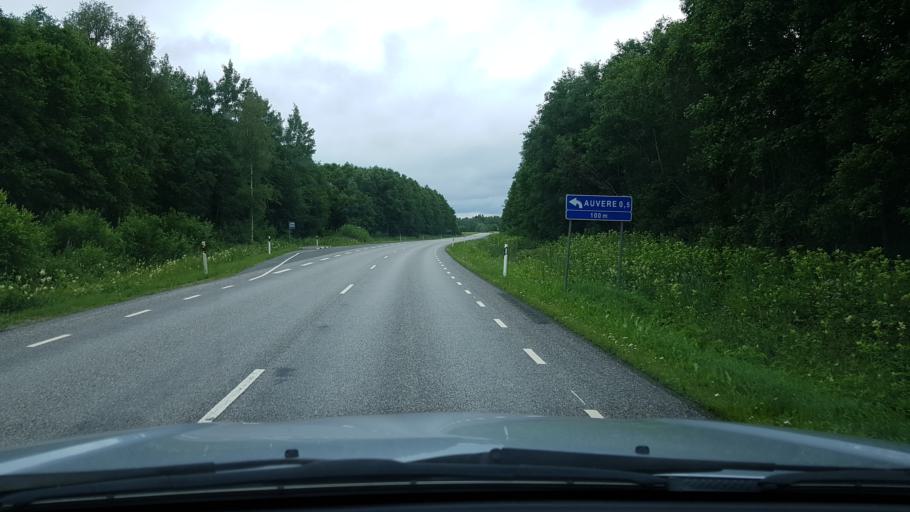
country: EE
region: Ida-Virumaa
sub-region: Narva-Joesuu linn
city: Narva-Joesuu
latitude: 59.3452
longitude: 27.9332
